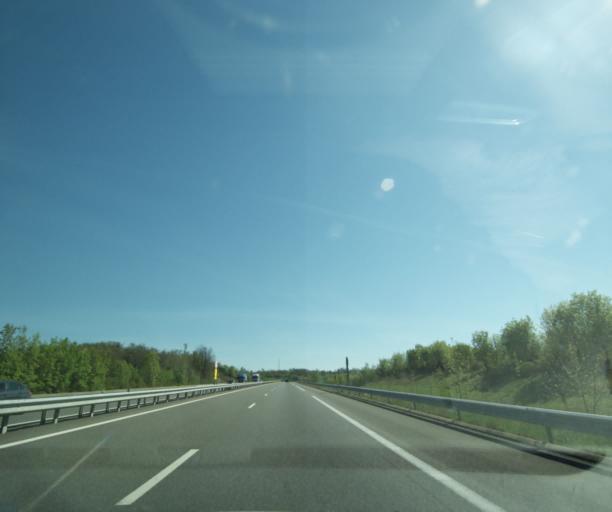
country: FR
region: Midi-Pyrenees
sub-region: Departement du Lot
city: Lalbenque
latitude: 44.2593
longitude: 1.5075
